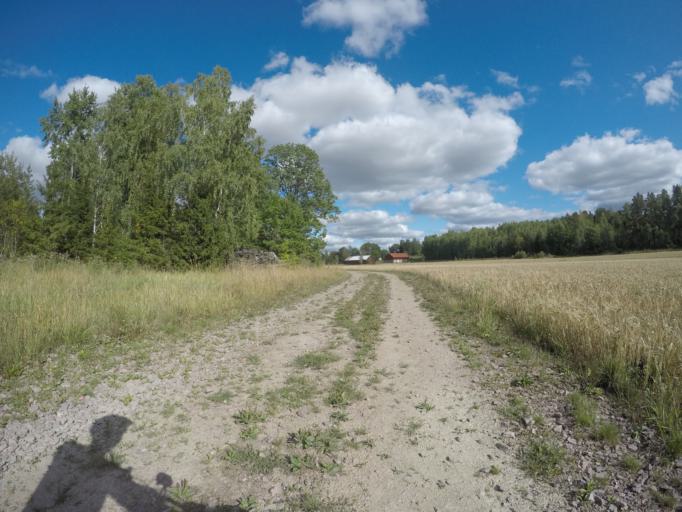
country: SE
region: Vaestmanland
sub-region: Hallstahammars Kommun
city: Kolback
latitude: 59.5170
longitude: 16.2009
